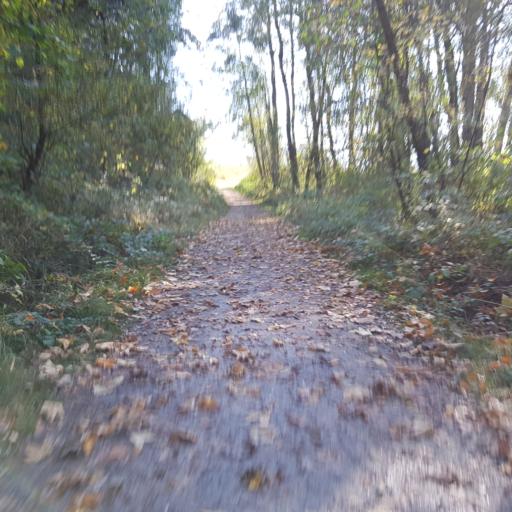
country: AT
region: Salzburg
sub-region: Politischer Bezirk Hallein
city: Hallein
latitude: 47.6719
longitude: 13.1159
